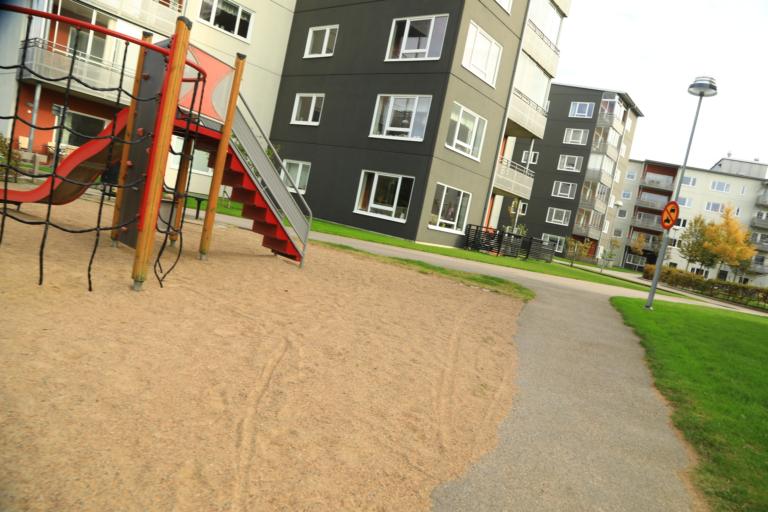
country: SE
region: Halland
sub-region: Varbergs Kommun
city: Traslovslage
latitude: 57.0879
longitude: 12.2748
